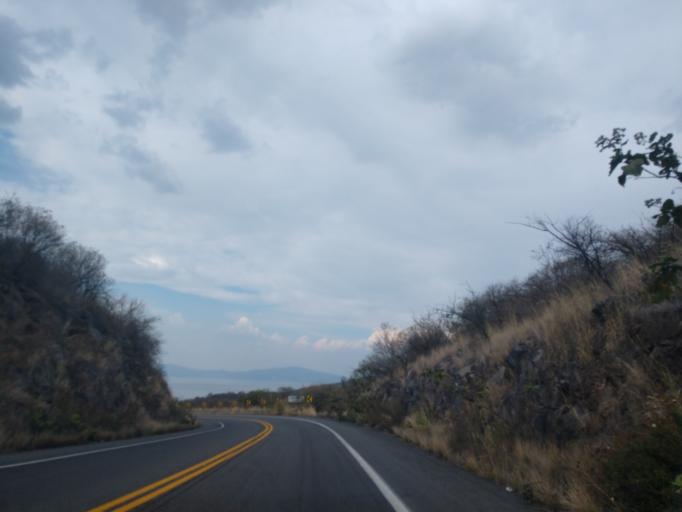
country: MX
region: Jalisco
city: La Manzanilla de la Paz
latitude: 20.1142
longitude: -103.1648
